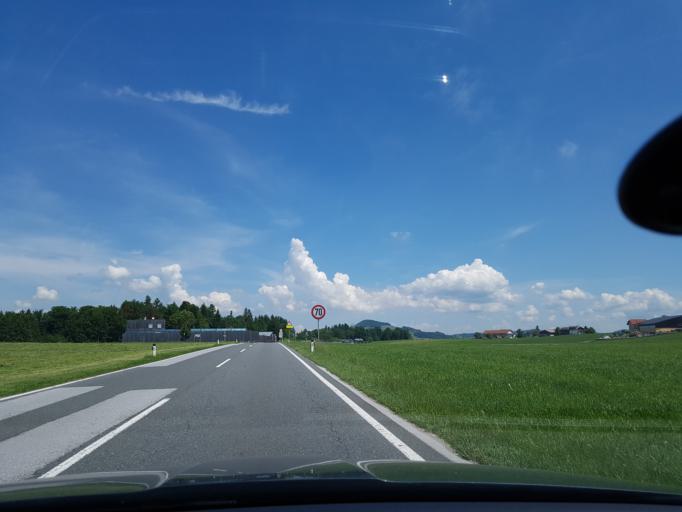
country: AT
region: Salzburg
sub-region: Politischer Bezirk Salzburg-Umgebung
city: Obertrum am See
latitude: 47.9044
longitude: 13.0798
